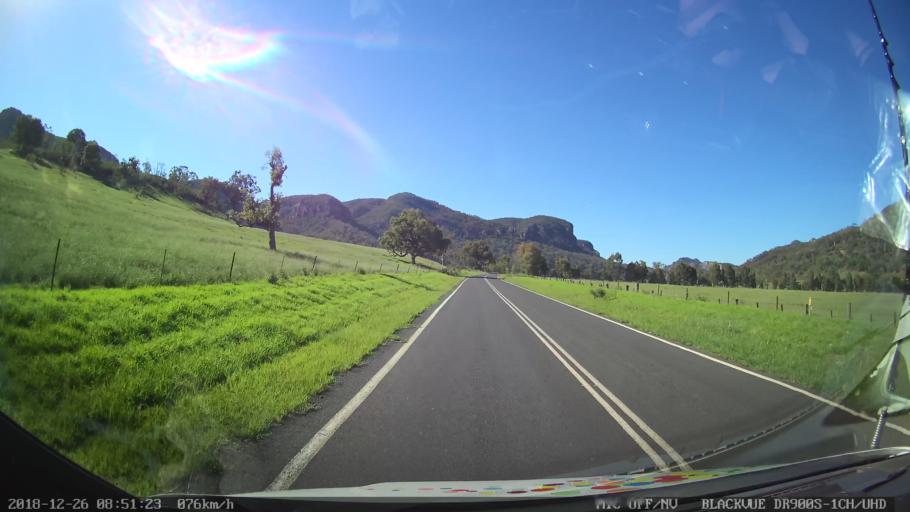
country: AU
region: New South Wales
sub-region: Mid-Western Regional
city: Kandos
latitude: -32.5843
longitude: 150.0889
